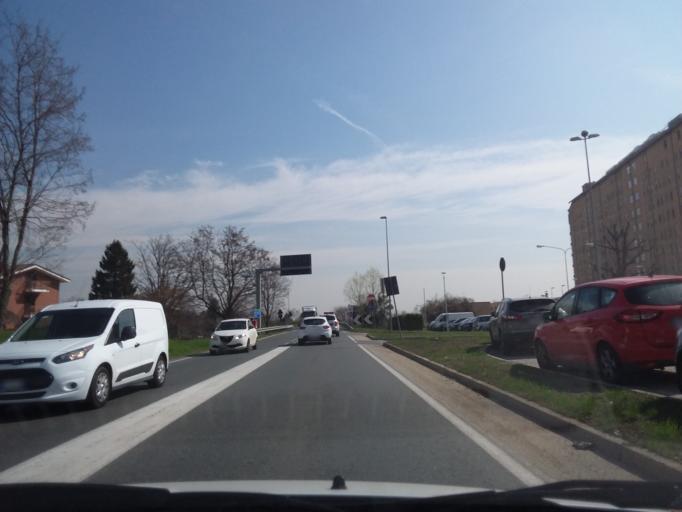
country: IT
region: Piedmont
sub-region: Provincia di Torino
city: Rivoli
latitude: 45.0604
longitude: 7.5200
